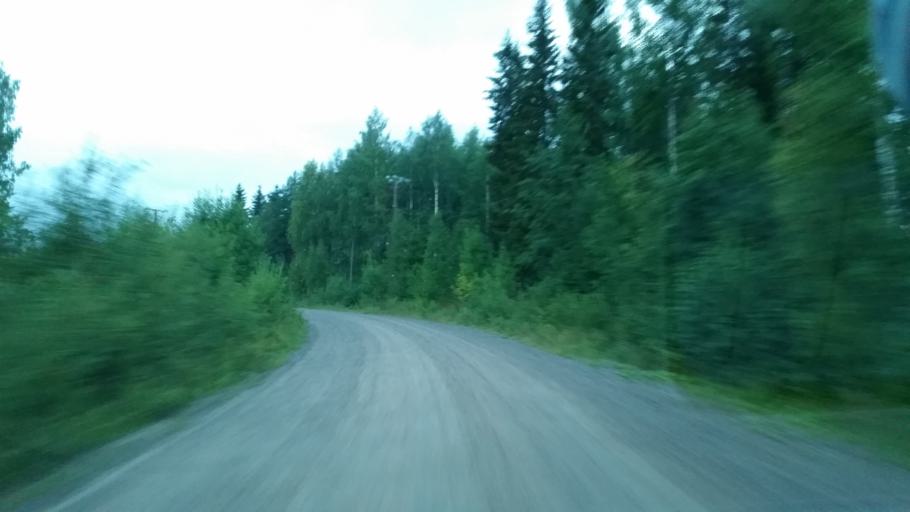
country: SE
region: Gaevleborg
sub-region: Ljusdals Kommun
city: Farila
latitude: 61.9177
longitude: 15.8436
